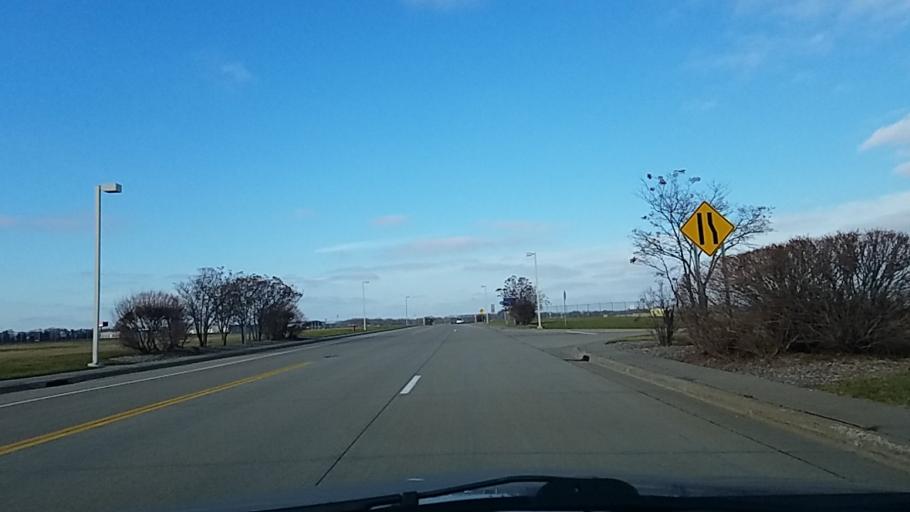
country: US
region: Minnesota
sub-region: Hennepin County
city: Richfield
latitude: 44.8797
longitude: -93.2366
